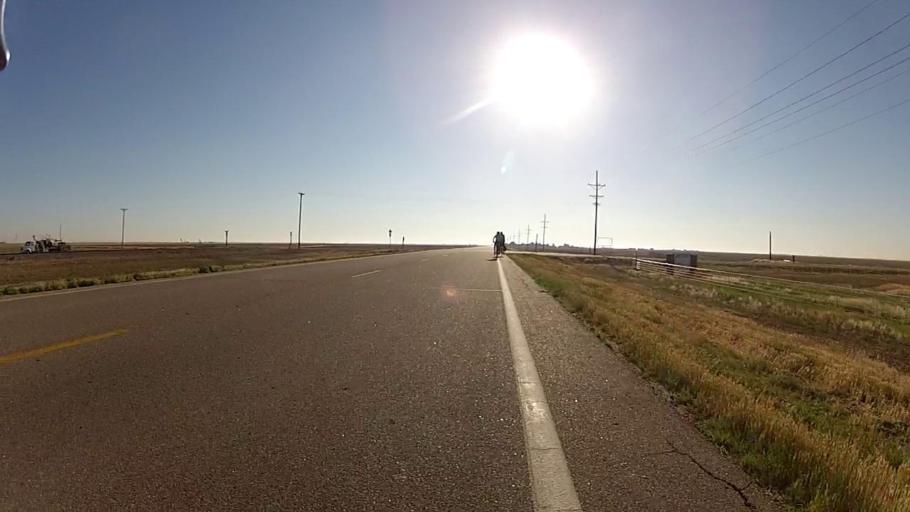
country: US
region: Kansas
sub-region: Haskell County
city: Sublette
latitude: 37.4908
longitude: -100.8172
